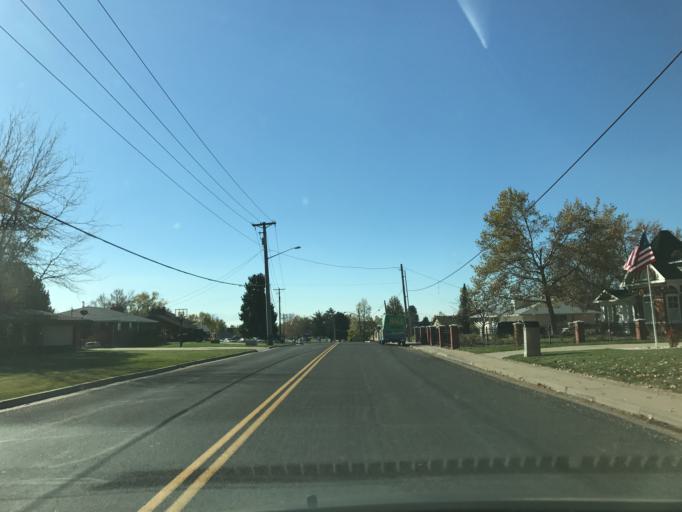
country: US
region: Utah
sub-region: Davis County
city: Layton
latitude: 41.0718
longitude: -111.9619
